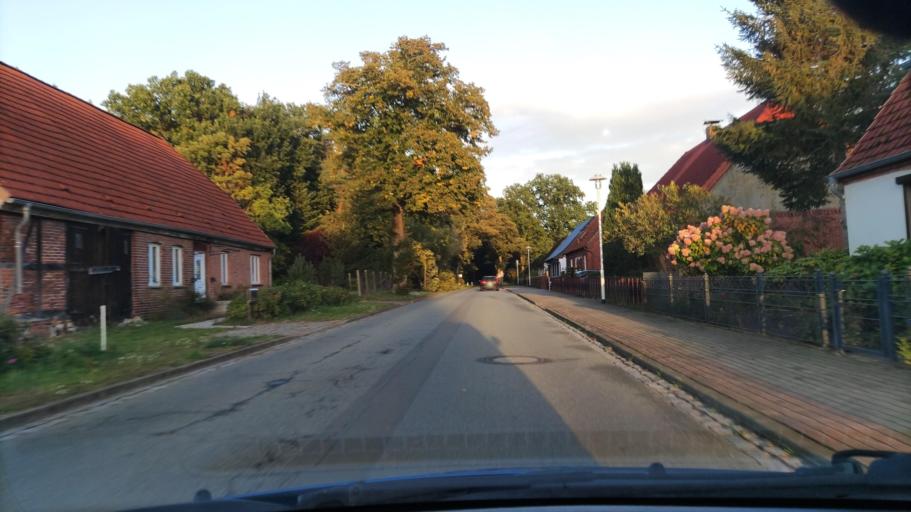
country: DE
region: Mecklenburg-Vorpommern
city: Lubtheen
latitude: 53.3178
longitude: 11.0259
